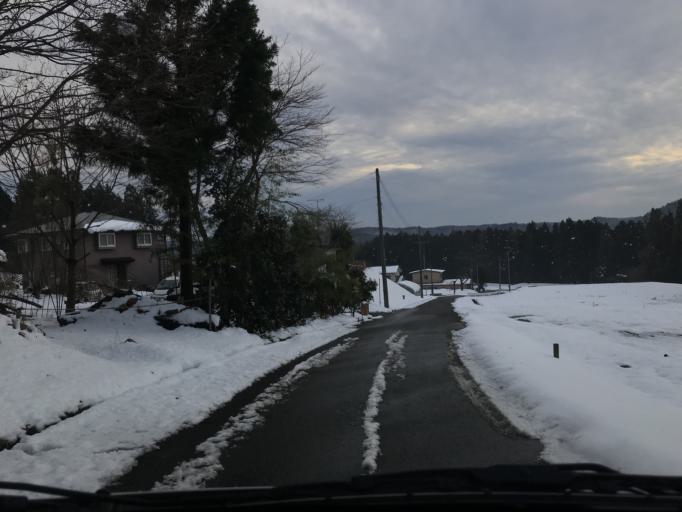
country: JP
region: Iwate
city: Mizusawa
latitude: 39.0497
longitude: 141.0577
